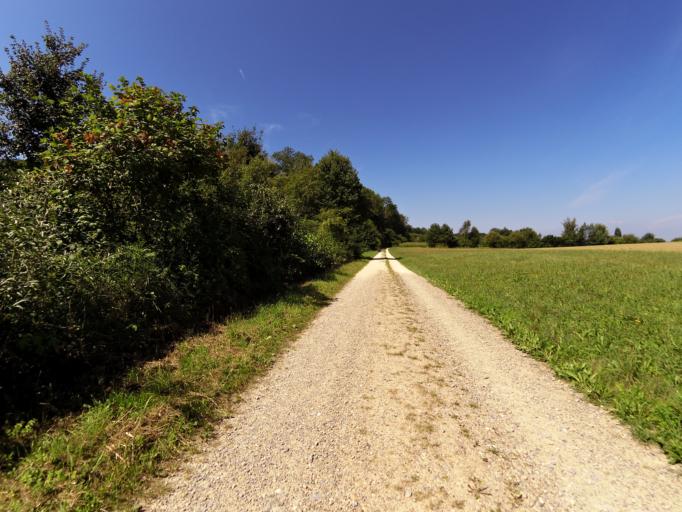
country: CH
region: Thurgau
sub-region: Kreuzlingen District
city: Tagerwilen
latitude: 47.6391
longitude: 9.1461
